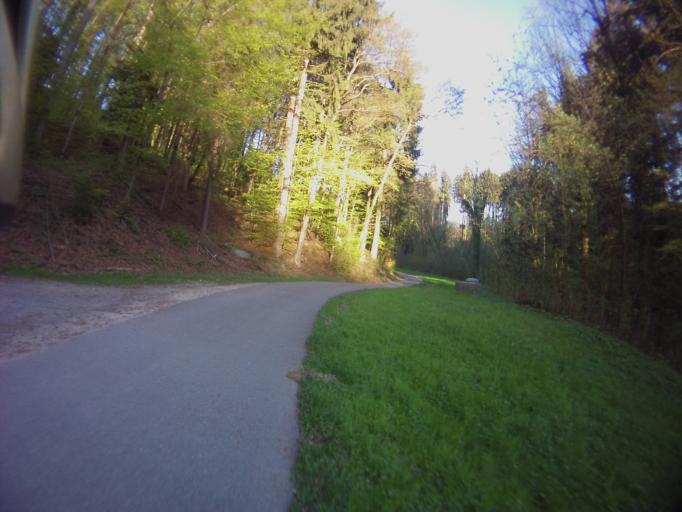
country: CH
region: Zurich
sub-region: Bezirk Dietikon
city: Birmensdorf
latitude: 47.3463
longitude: 8.4558
